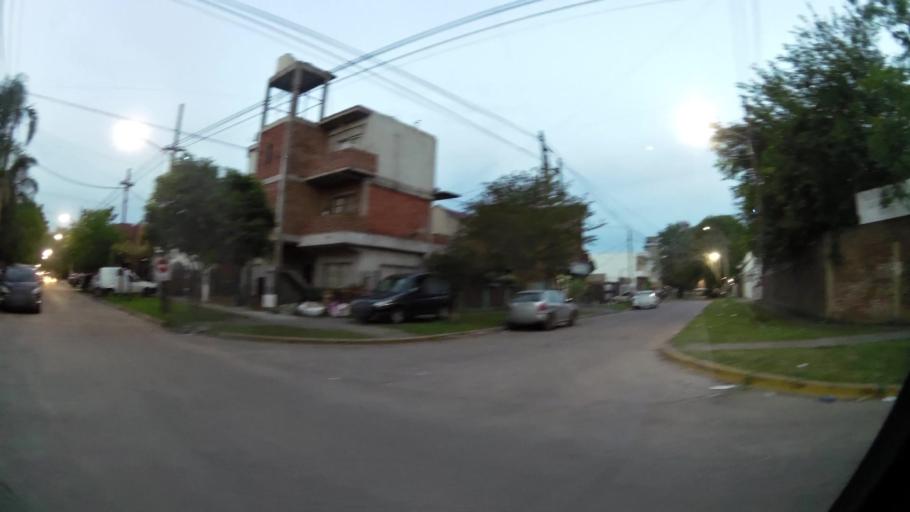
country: AR
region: Buenos Aires
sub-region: Partido de Quilmes
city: Quilmes
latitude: -34.8019
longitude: -58.2803
